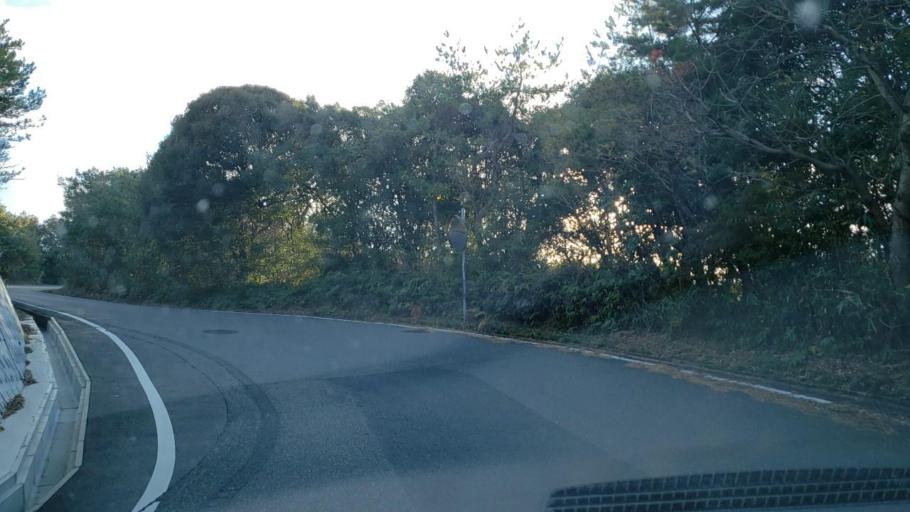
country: JP
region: Hyogo
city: Akashi
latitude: 34.5406
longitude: 134.9629
